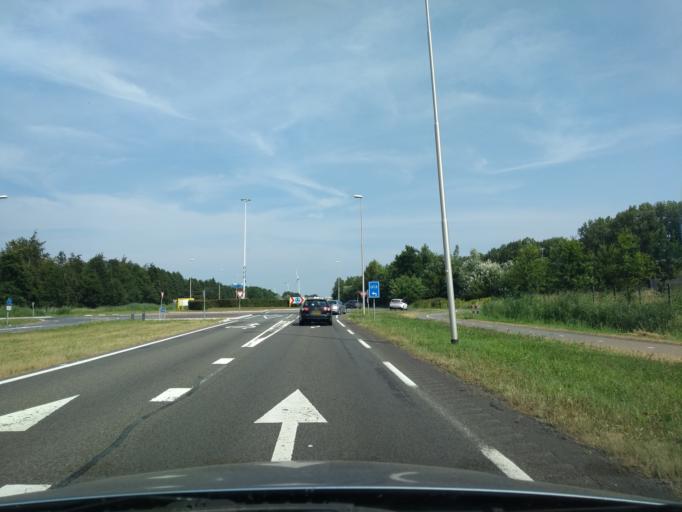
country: NL
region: Flevoland
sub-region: Gemeente Lelystad
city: Lelystad
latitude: 52.5492
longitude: 5.5132
